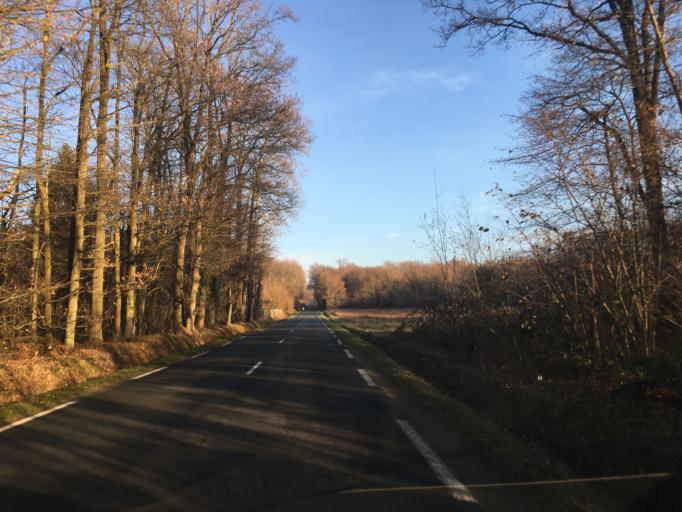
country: FR
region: Haute-Normandie
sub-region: Departement de l'Eure
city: Houlbec-Cocherel
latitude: 49.0647
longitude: 1.3794
